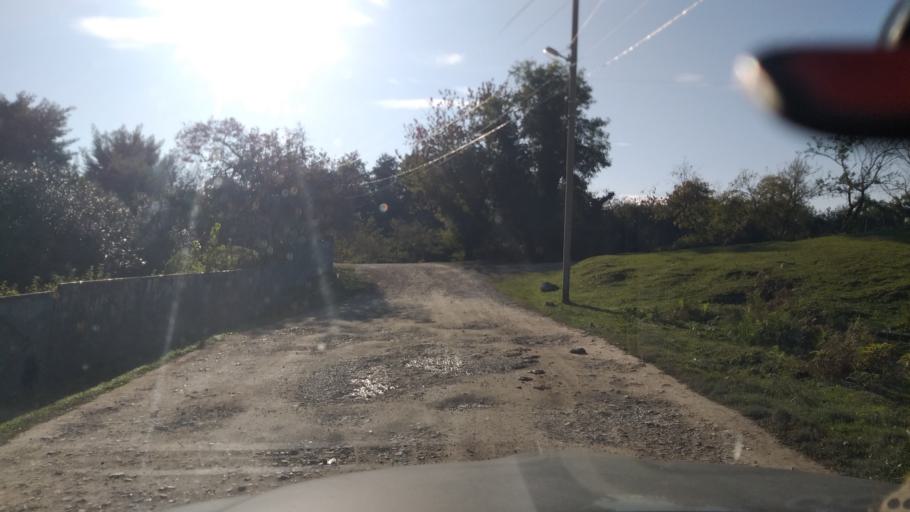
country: GE
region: Abkhazia
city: Stantsiya Novyy Afon
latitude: 43.0617
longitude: 40.8909
